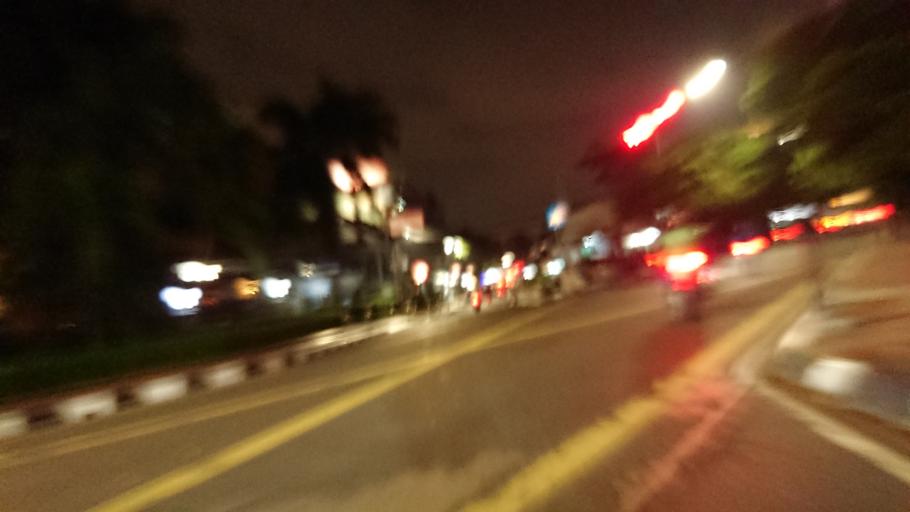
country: ID
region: Jakarta Raya
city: Jakarta
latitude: -6.2095
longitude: 106.7965
